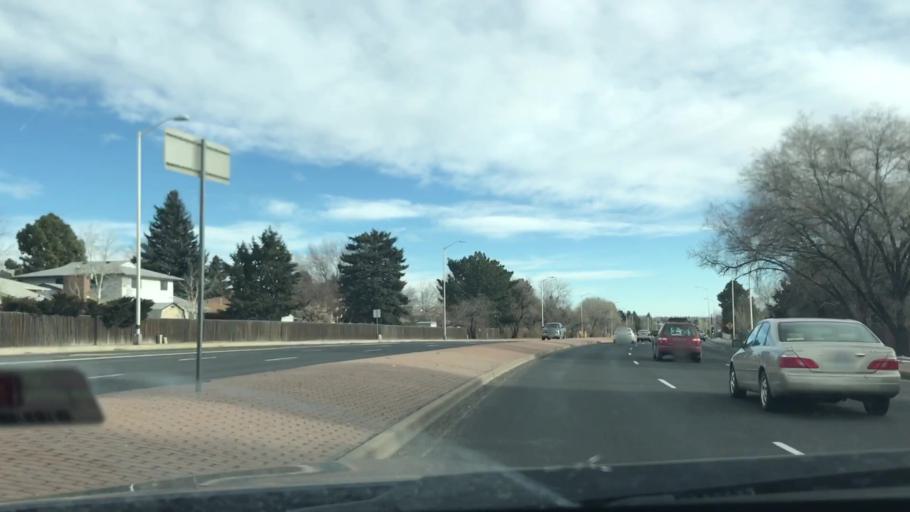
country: US
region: Colorado
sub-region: El Paso County
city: Cimarron Hills
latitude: 38.8999
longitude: -104.7644
